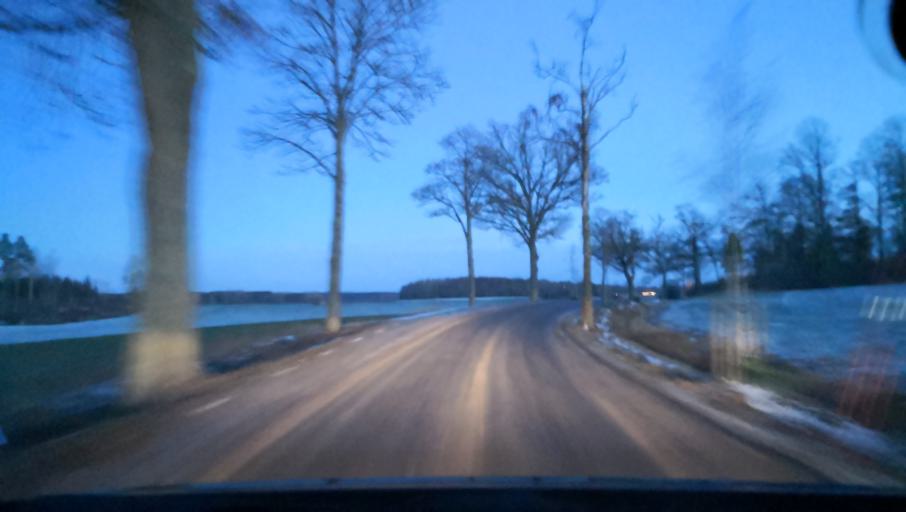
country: SE
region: Soedermanland
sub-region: Katrineholms Kommun
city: Katrineholm
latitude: 59.0768
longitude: 16.3304
